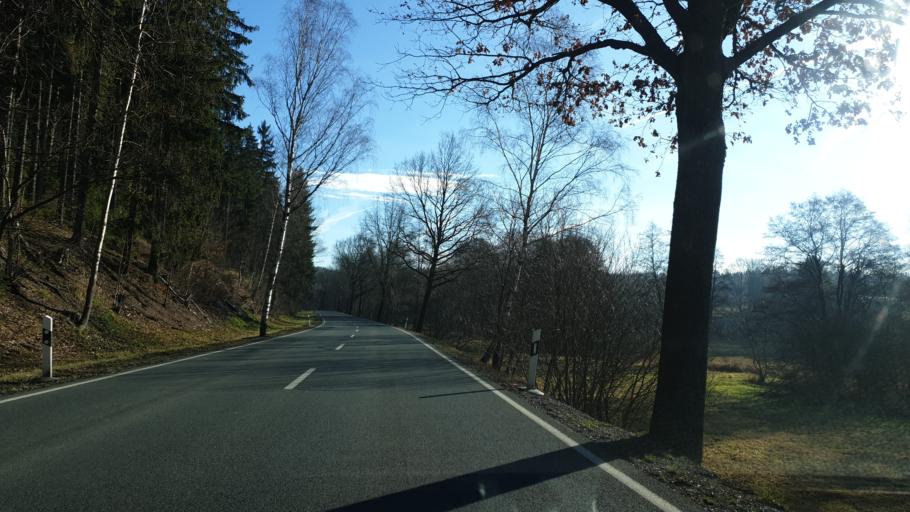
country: DE
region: Saxony
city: Adorf
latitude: 50.2802
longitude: 12.2824
